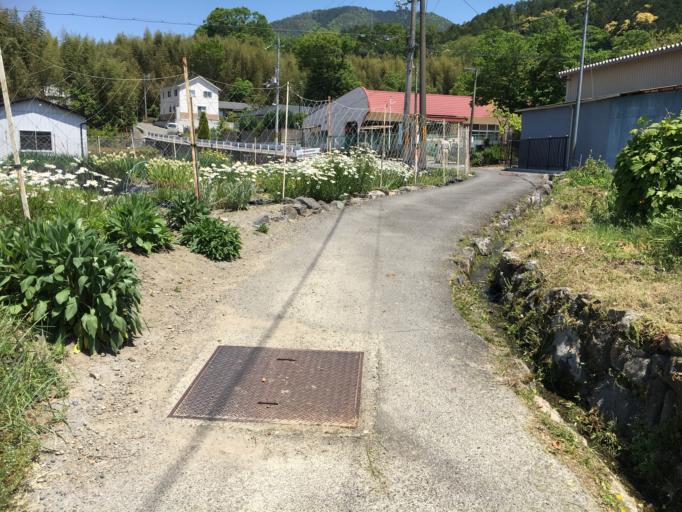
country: JP
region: Kyoto
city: Kameoka
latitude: 35.0244
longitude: 135.5930
